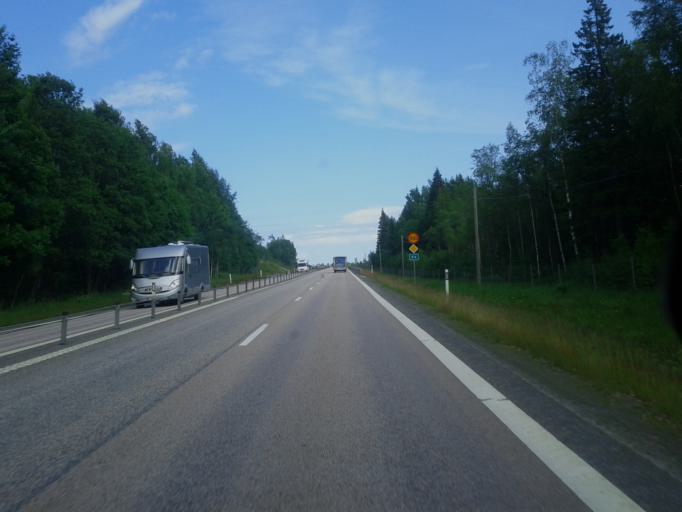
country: SE
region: Vaesternorrland
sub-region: OErnskoeldsviks Kommun
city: Husum
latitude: 63.3633
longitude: 19.1798
